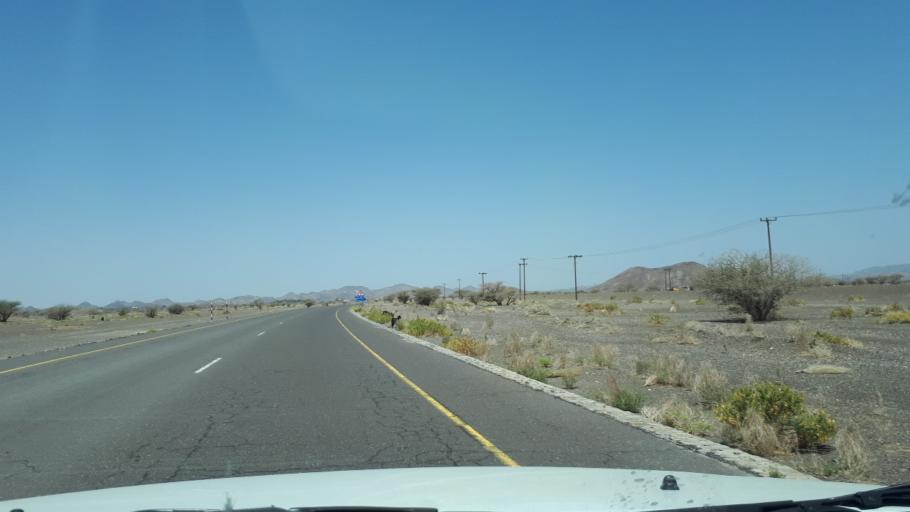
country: OM
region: Ash Sharqiyah
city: Ibra'
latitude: 22.6177
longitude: 58.4194
